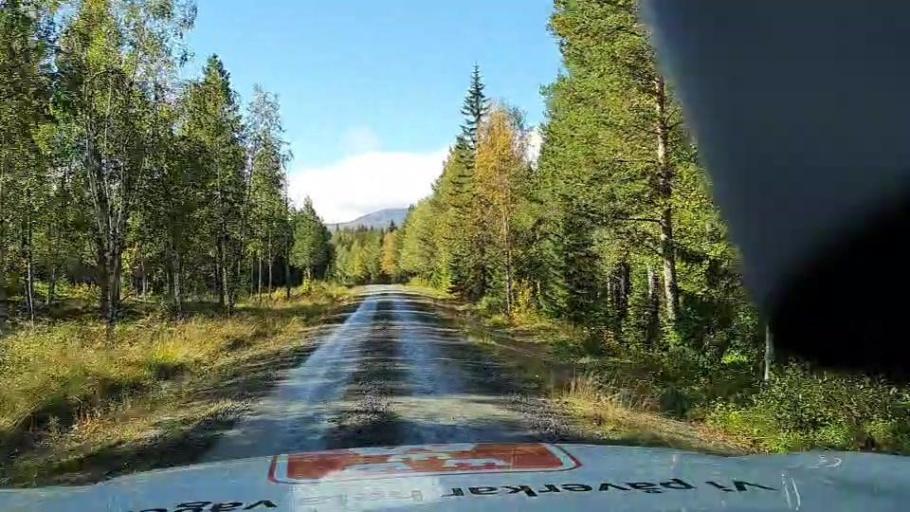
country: SE
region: Jaemtland
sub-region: Are Kommun
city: Are
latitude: 63.1902
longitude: 13.1750
